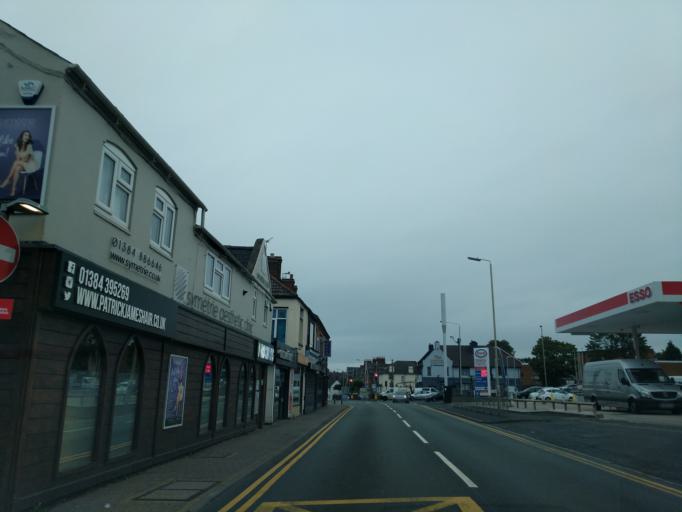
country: GB
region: England
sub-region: Dudley
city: Stourbridge
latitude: 52.4477
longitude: -2.1406
